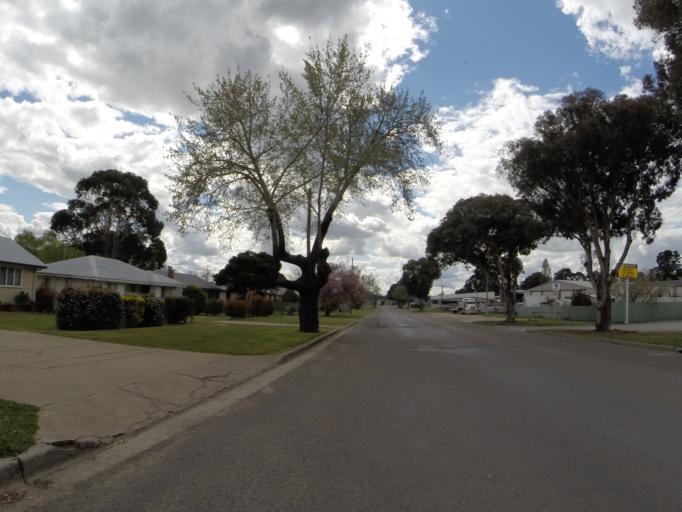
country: AU
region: New South Wales
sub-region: Yass Valley
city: Yass
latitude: -34.8527
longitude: 148.9184
